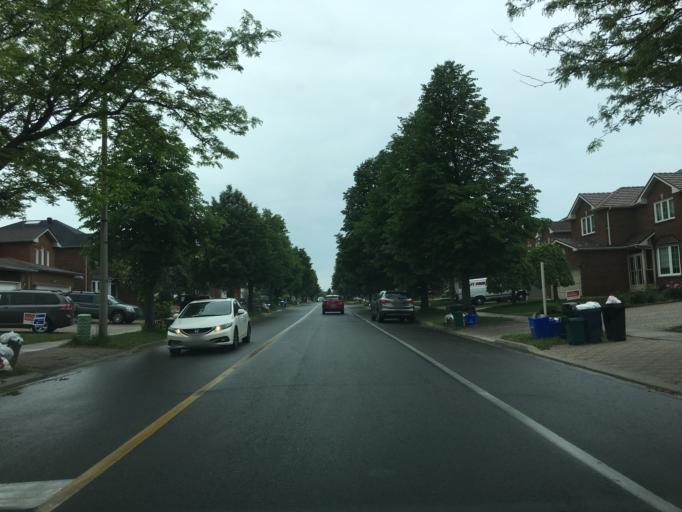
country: CA
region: Ontario
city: Markham
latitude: 43.8371
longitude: -79.2624
